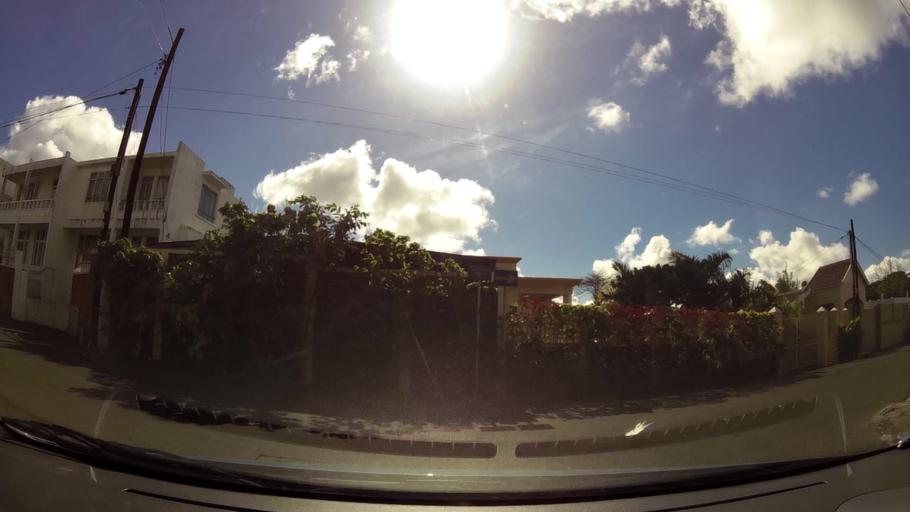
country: MU
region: Plaines Wilhems
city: Curepipe
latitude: -20.3235
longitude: 57.5323
